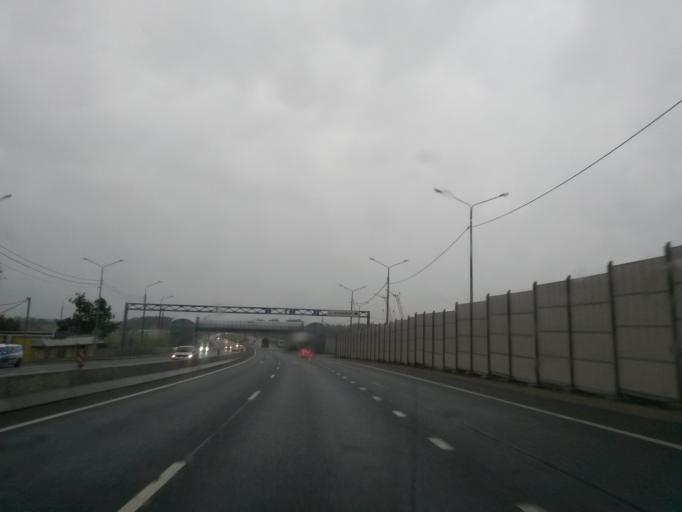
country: RU
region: Jaroslavl
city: Yaroslavl
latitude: 57.7045
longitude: 39.9002
